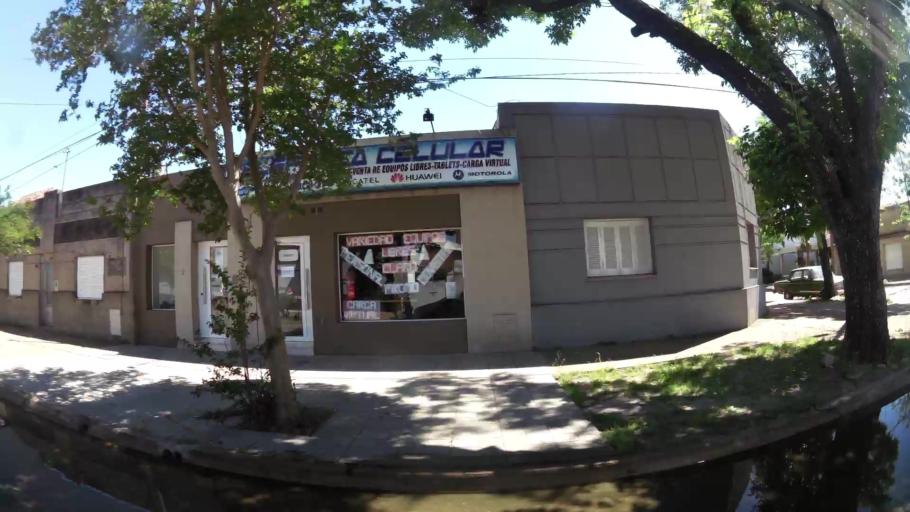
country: AR
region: Santa Fe
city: Esperanza
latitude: -31.4451
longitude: -60.9273
